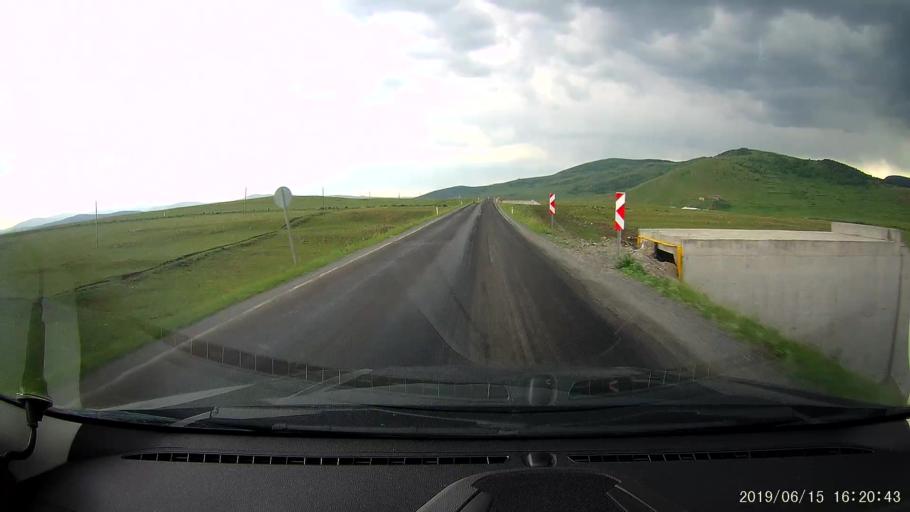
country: TR
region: Ardahan
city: Hanak
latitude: 41.2095
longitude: 42.8467
